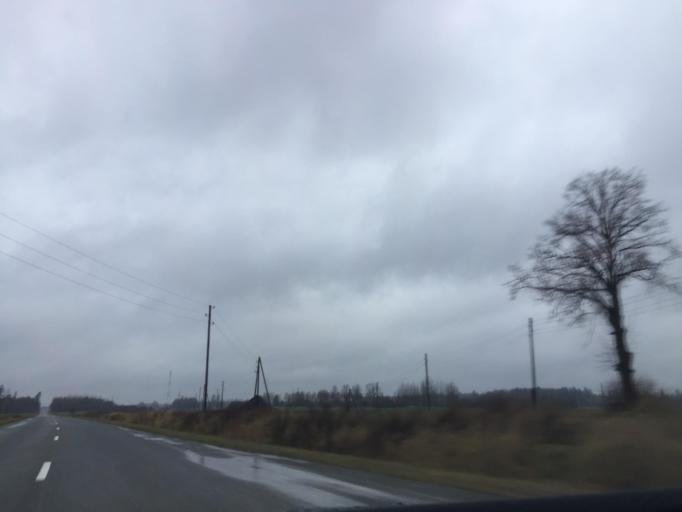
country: LV
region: Aloja
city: Staicele
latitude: 57.7598
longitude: 24.5675
